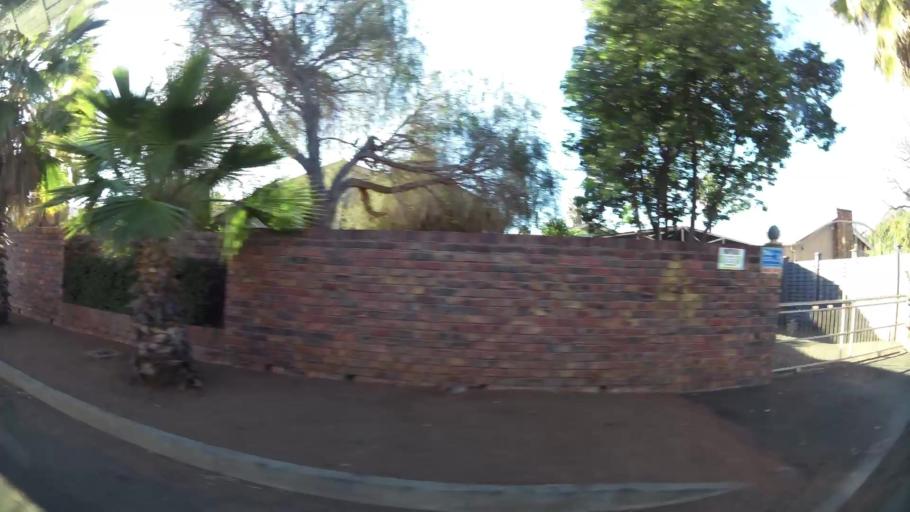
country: ZA
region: Northern Cape
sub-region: Frances Baard District Municipality
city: Kimberley
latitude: -28.7384
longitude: 24.7321
